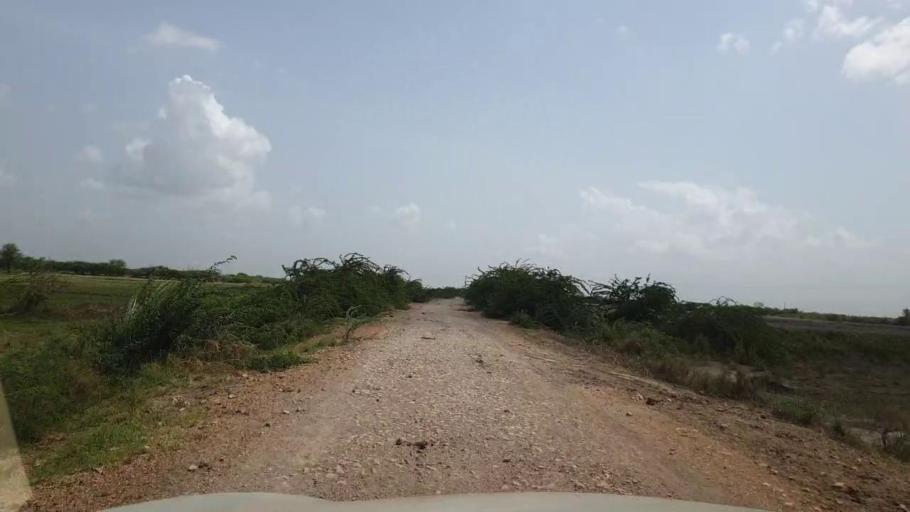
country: PK
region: Sindh
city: Kadhan
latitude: 24.3999
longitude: 68.7978
